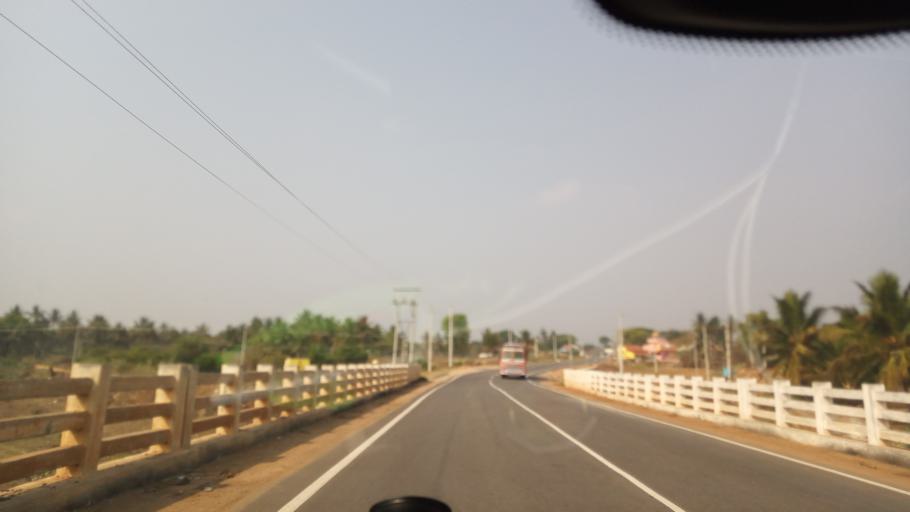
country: IN
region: Karnataka
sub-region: Mandya
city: Melukote
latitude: 12.7137
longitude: 76.7062
